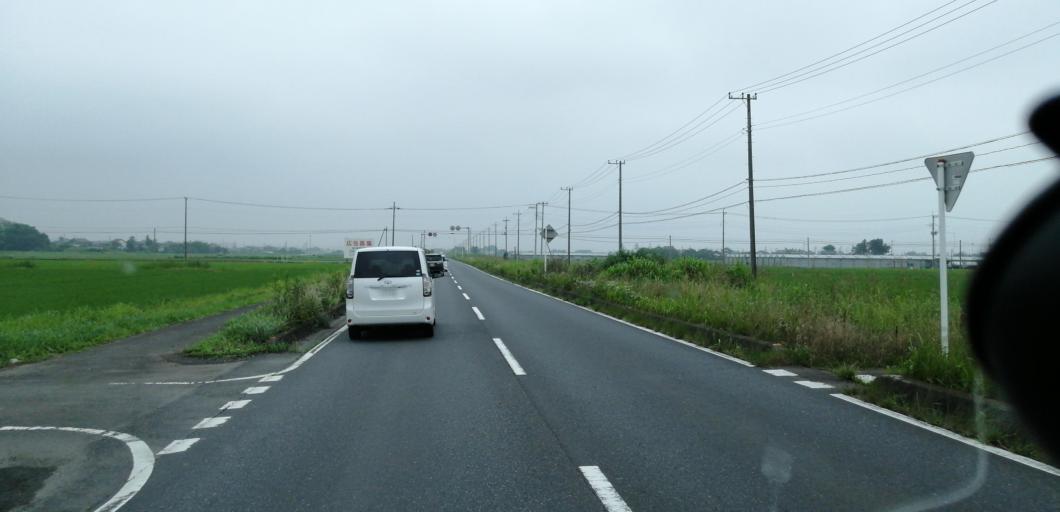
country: JP
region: Saitama
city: Kazo
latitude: 36.1417
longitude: 139.5834
